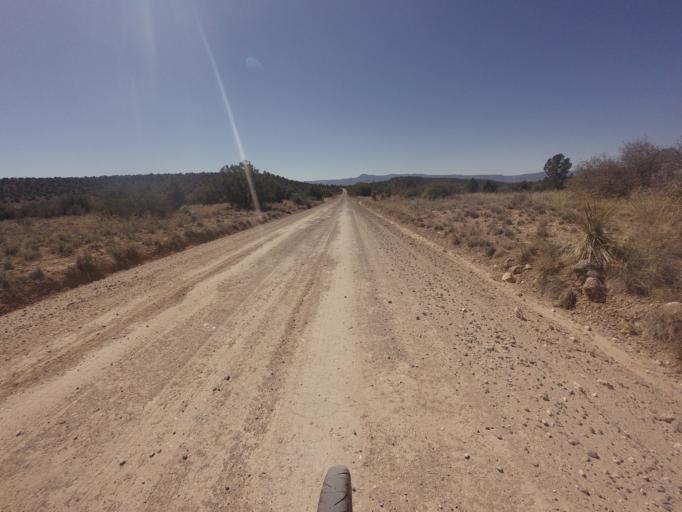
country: US
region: Arizona
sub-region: Yavapai County
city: Lake Montezuma
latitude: 34.5955
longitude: -111.7278
